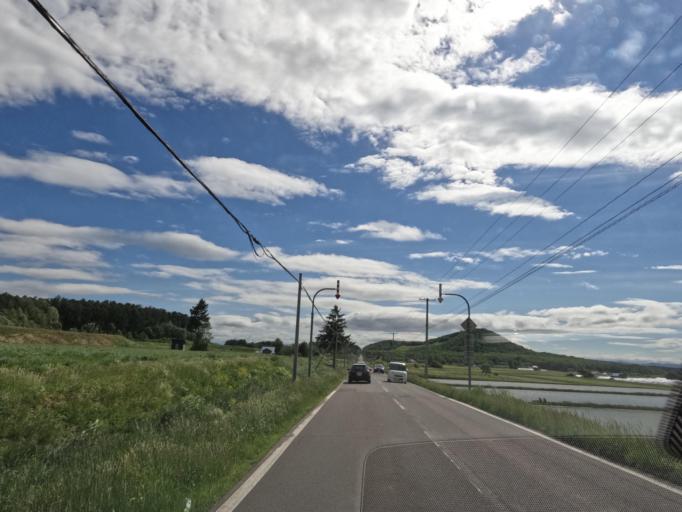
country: JP
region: Hokkaido
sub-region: Asahikawa-shi
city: Asahikawa
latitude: 43.8450
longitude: 142.5525
